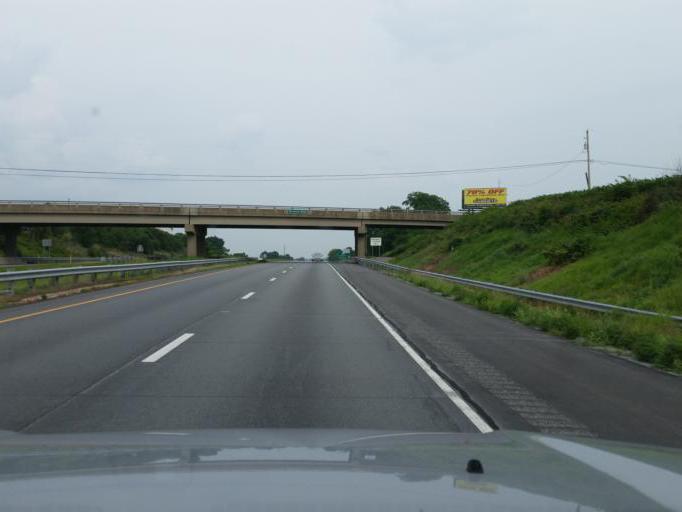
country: US
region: Pennsylvania
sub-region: Lancaster County
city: Mount Joy
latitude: 40.1283
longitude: -76.4770
